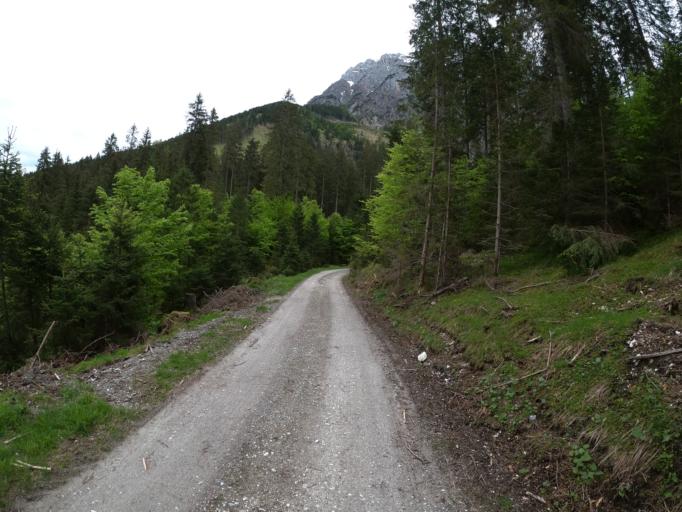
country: AT
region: Salzburg
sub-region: Politischer Bezirk Sankt Johann im Pongau
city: Werfen
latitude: 47.4685
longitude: 13.0796
